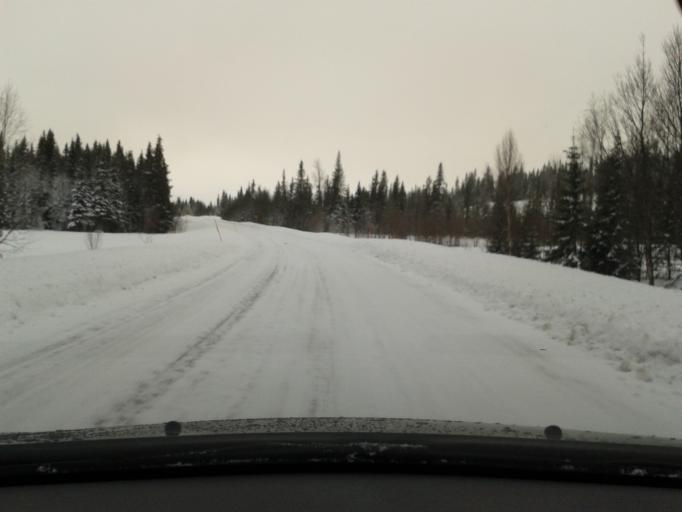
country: SE
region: Vaesterbotten
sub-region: Vilhelmina Kommun
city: Sjoberg
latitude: 65.1998
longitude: 15.9772
